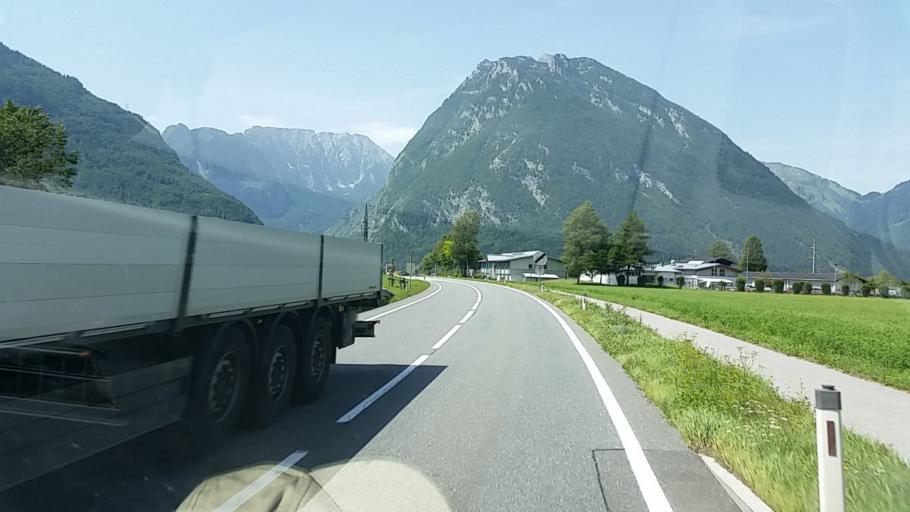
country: AT
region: Salzburg
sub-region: Politischer Bezirk Hallein
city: Golling an der Salzach
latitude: 47.5909
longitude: 13.1843
